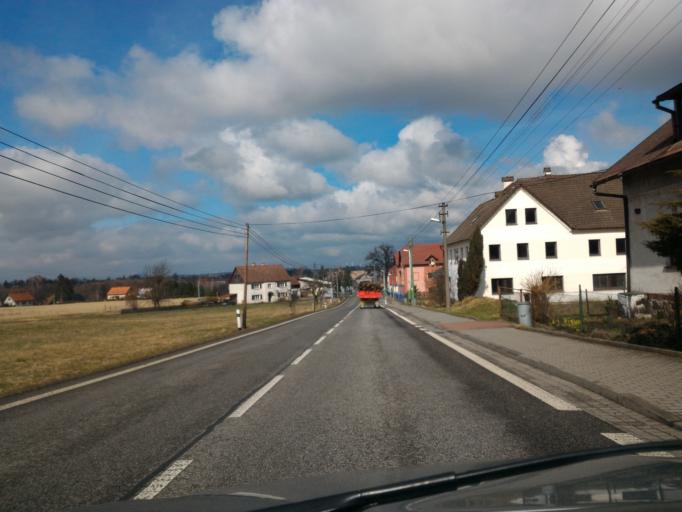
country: PL
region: Silesian Voivodeship
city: Zawidow
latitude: 51.0174
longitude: 15.0657
